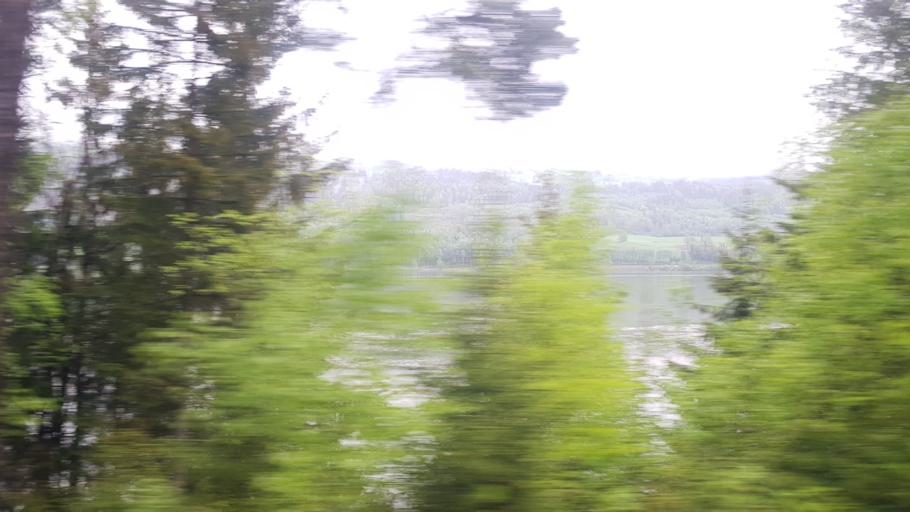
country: NO
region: Oppland
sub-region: Oyer
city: Tretten
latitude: 61.3894
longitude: 10.2549
